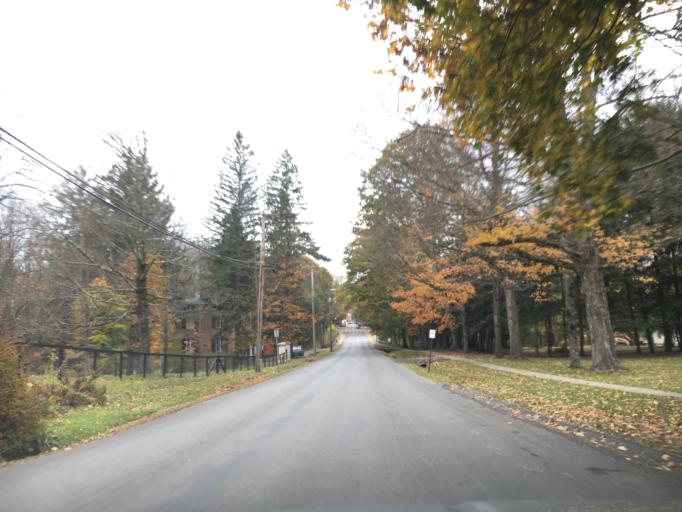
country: US
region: New York
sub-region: Otsego County
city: Cooperstown
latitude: 42.6992
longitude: -74.9184
